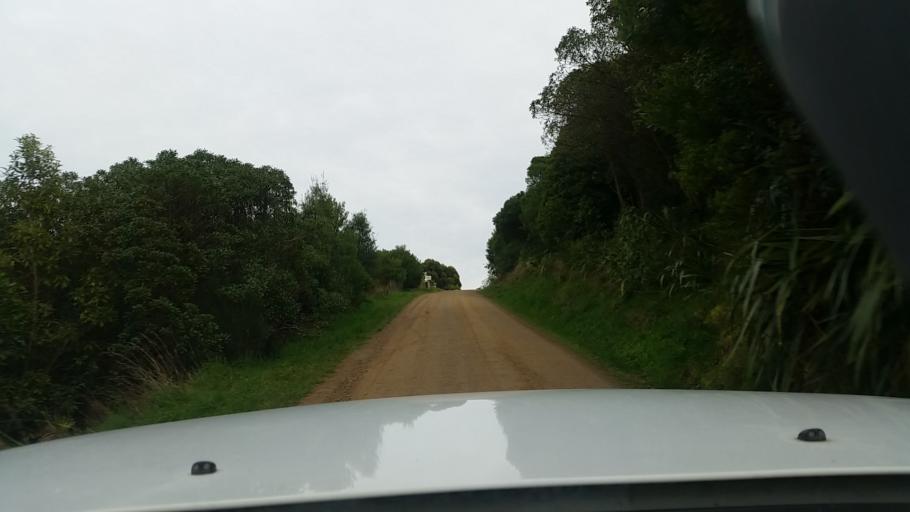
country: NZ
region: Canterbury
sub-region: Christchurch City
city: Christchurch
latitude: -43.6346
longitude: 172.7394
